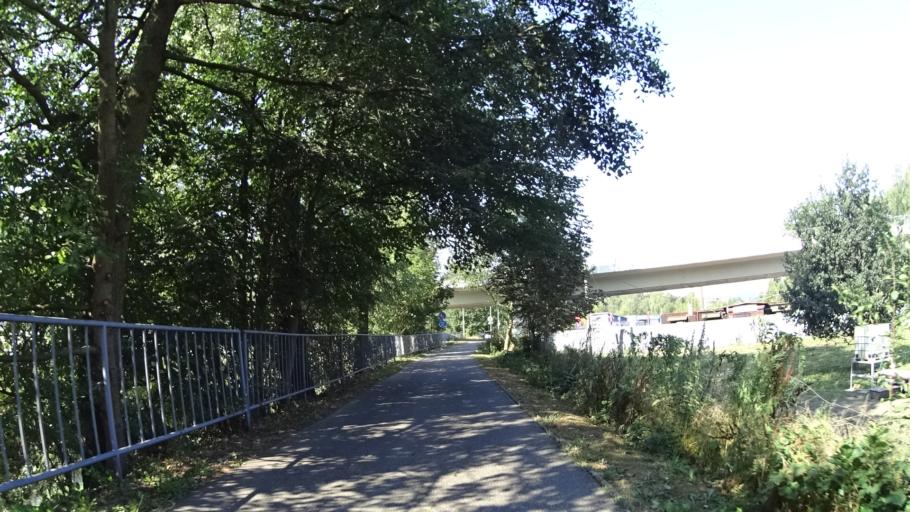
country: CZ
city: Straz nad Nisou
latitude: 50.7793
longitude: 15.0404
